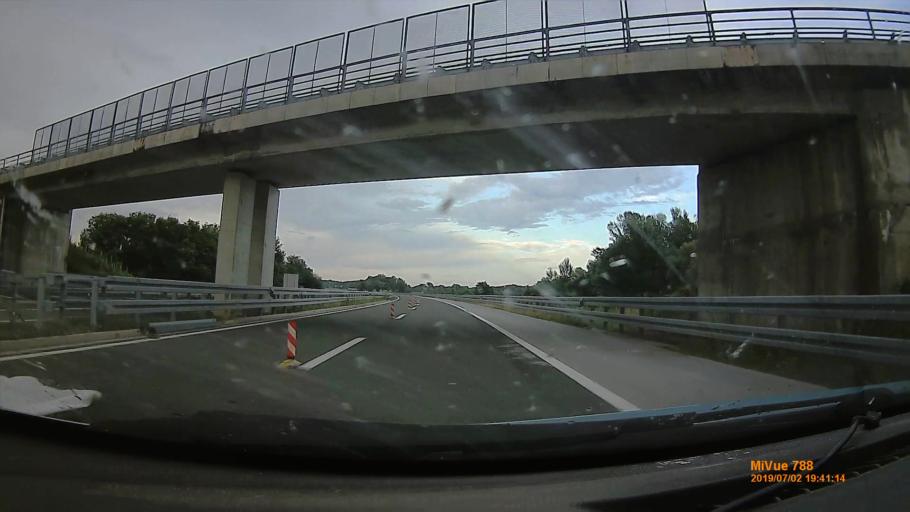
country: HR
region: Medimurska
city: Gorican
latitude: 46.4075
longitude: 16.6854
